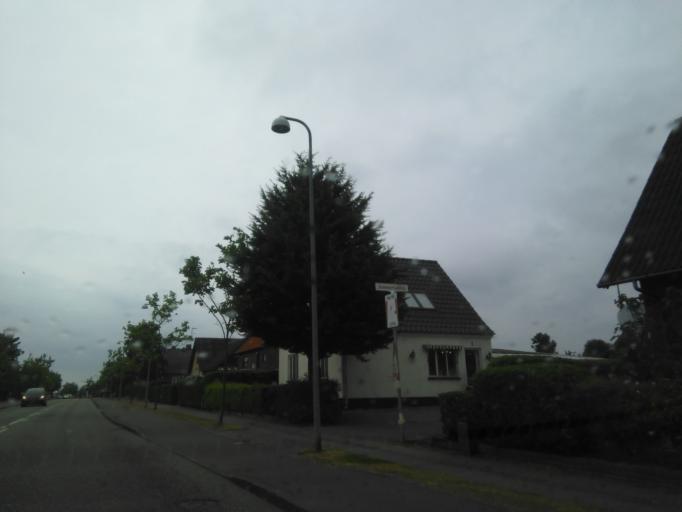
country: DK
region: Capital Region
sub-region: Bornholm Kommune
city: Ronne
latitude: 55.0941
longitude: 14.7237
